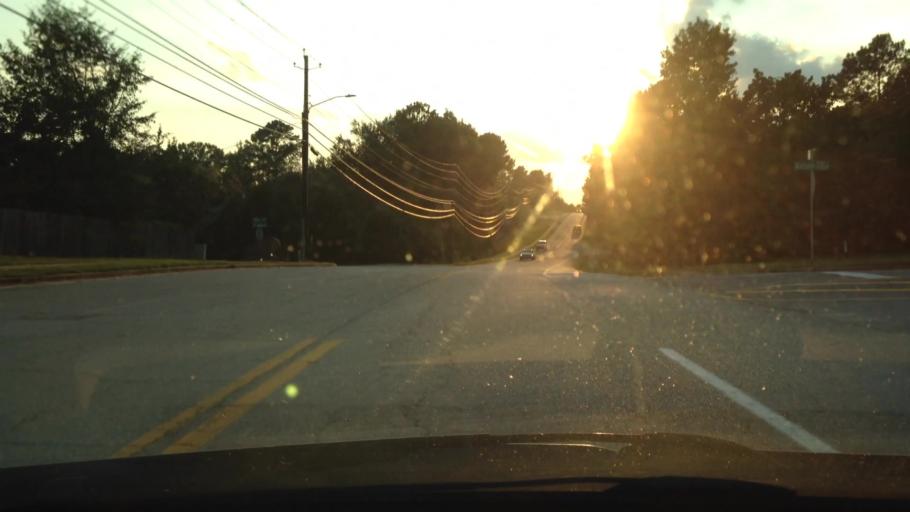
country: US
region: Alabama
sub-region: Russell County
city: Phenix City
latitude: 32.5560
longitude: -84.9794
